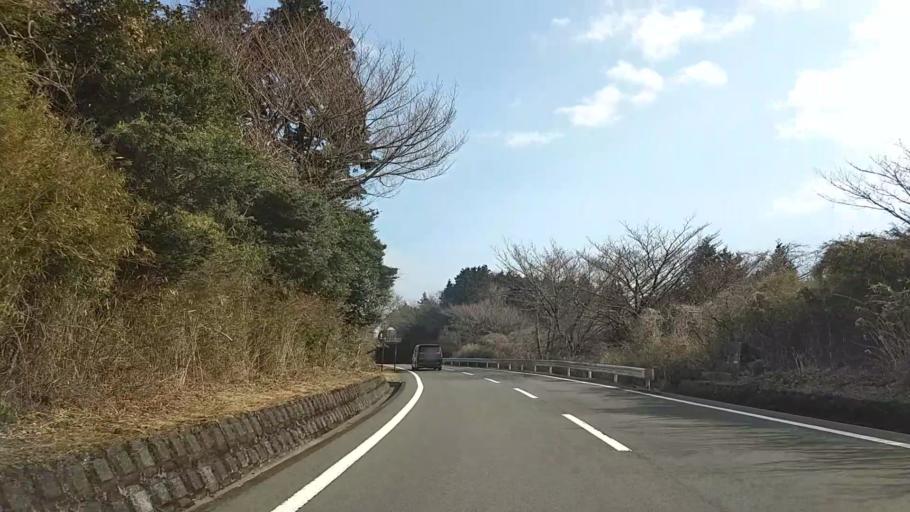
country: JP
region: Shizuoka
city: Atami
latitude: 35.0352
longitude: 139.0379
